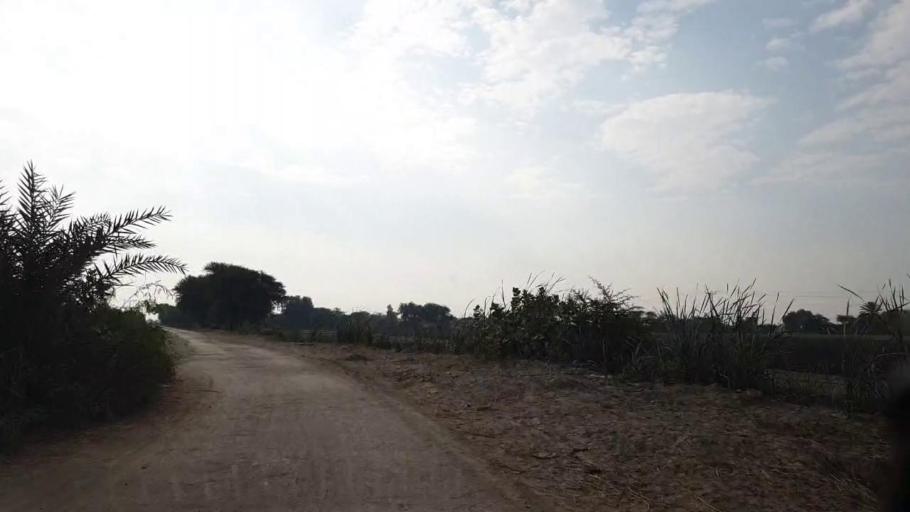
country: PK
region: Sindh
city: Tando Muhammad Khan
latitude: 25.0362
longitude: 68.4361
